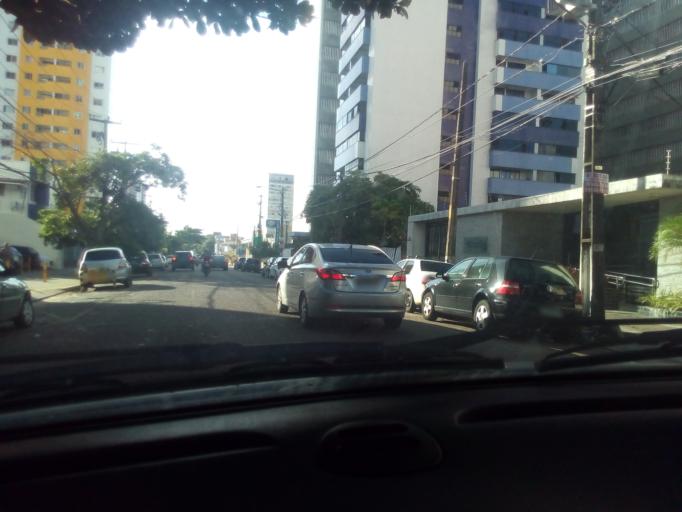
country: BR
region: Rio Grande do Norte
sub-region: Natal
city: Natal
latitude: -5.7906
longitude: -35.2032
